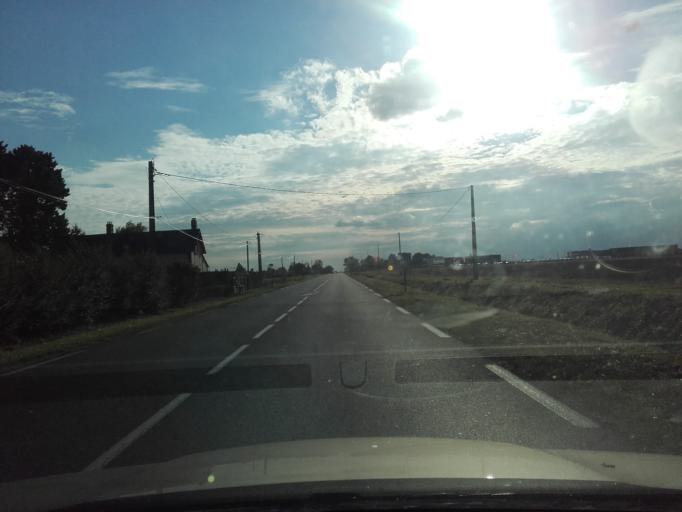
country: FR
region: Centre
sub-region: Departement d'Indre-et-Loire
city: Parcay-Meslay
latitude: 47.4701
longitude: 0.7519
